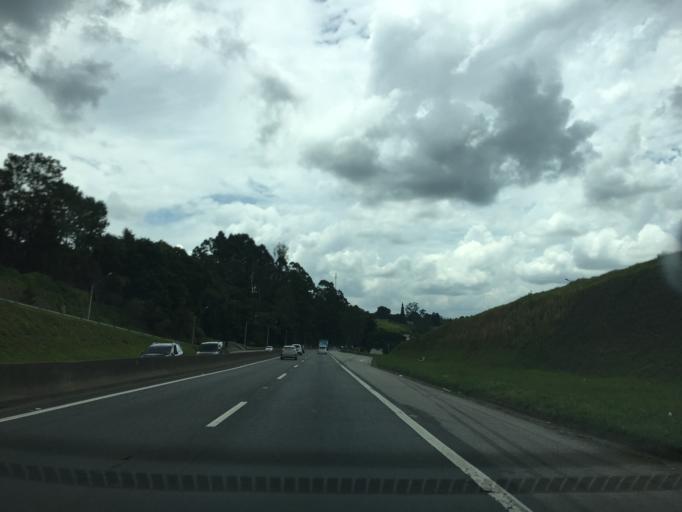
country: BR
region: Sao Paulo
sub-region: Mairipora
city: Mairipora
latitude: -23.2450
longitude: -46.5953
